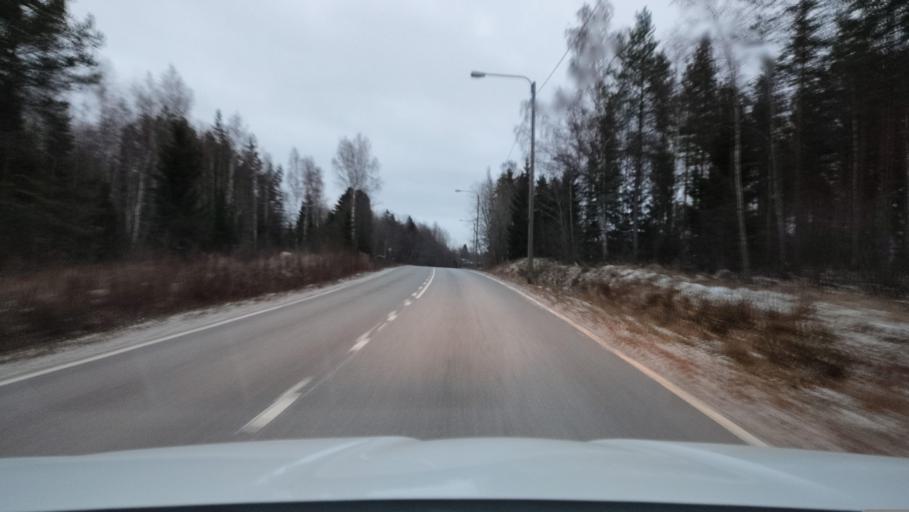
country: FI
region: Ostrobothnia
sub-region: Vaasa
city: Replot
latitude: 63.2354
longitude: 21.3999
